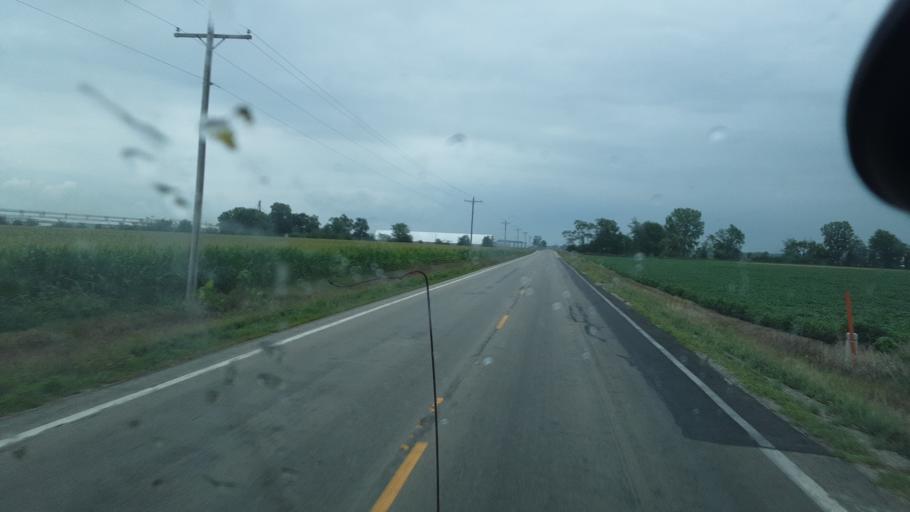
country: US
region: Ohio
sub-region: Defiance County
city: Hicksville
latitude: 41.2960
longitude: -84.7027
